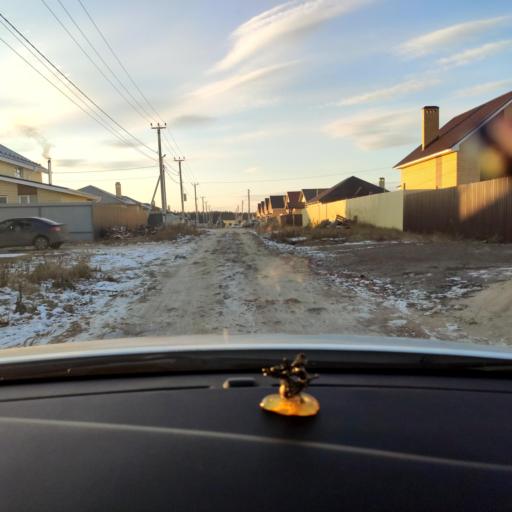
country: RU
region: Tatarstan
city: Stolbishchi
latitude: 55.6036
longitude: 49.1413
